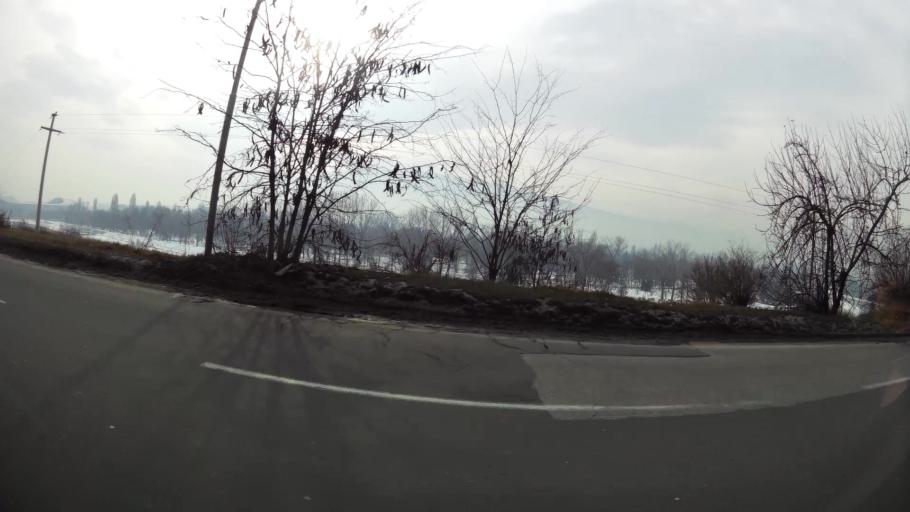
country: MK
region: Karpos
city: Skopje
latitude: 42.0135
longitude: 21.4192
